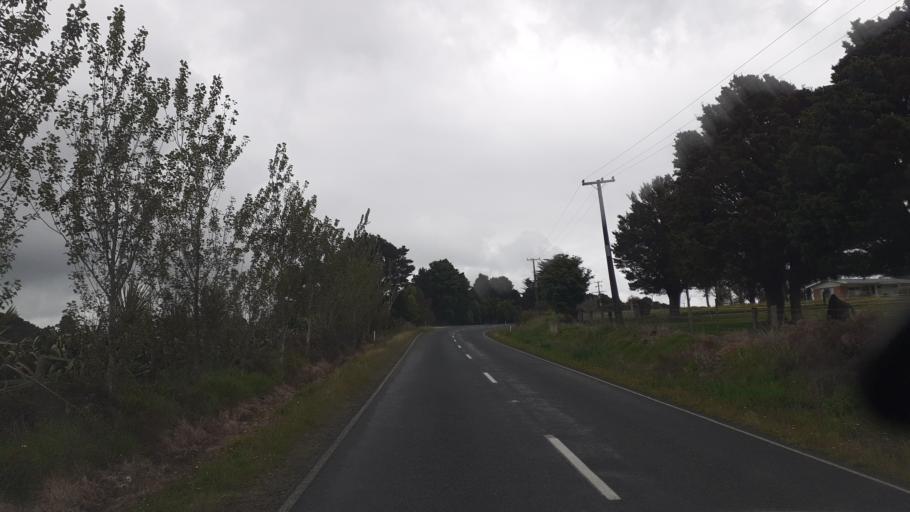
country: NZ
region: Northland
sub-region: Far North District
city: Waimate North
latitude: -35.2751
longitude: 173.8296
